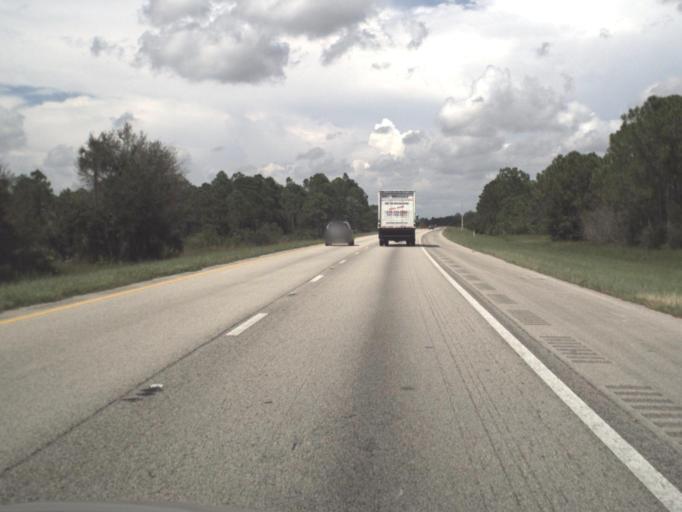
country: US
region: Florida
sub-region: Lee County
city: Suncoast Estates
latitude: 26.7835
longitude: -81.8978
